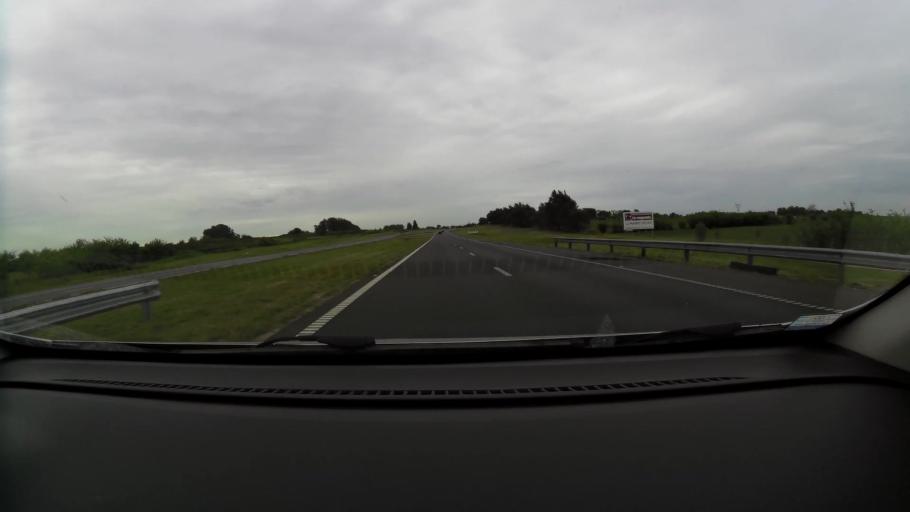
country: AR
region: Buenos Aires
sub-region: San Antonio de Areco
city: San Antonio de Areco
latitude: -34.0558
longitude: -59.3037
